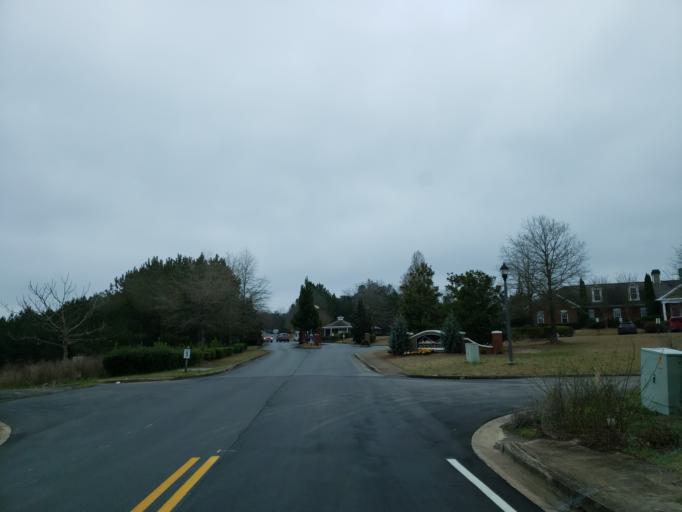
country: US
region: Georgia
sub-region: Pickens County
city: Jasper
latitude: 34.4437
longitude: -84.4473
